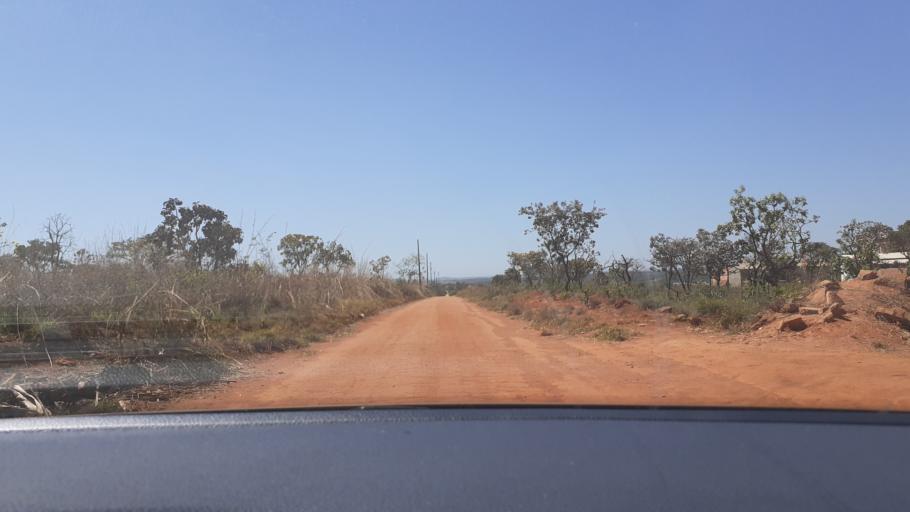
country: BR
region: Goias
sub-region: Aparecida De Goiania
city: Aparecida de Goiania
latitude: -16.8723
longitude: -49.2743
